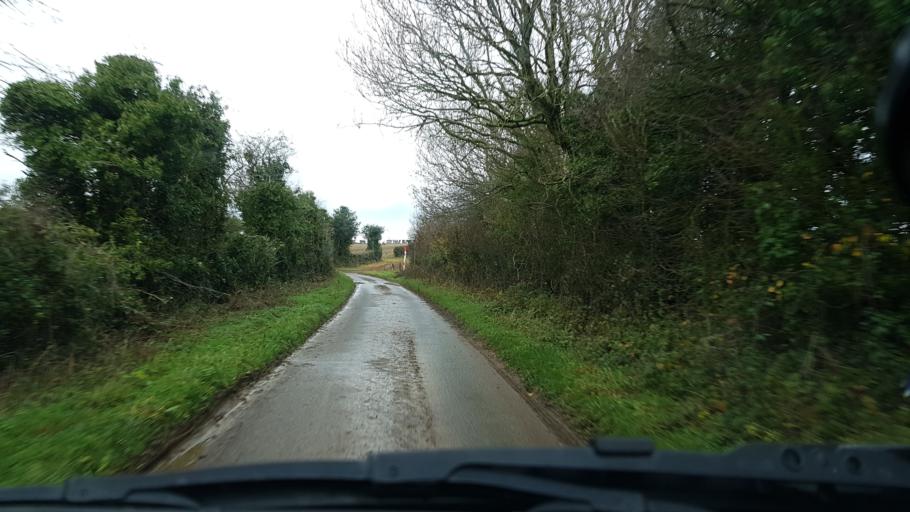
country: GB
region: England
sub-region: Gloucestershire
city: Charlton Kings
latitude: 51.8433
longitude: -2.0293
